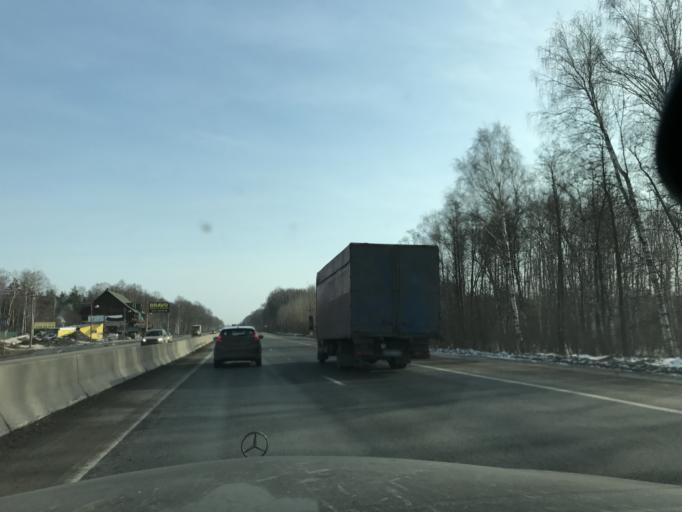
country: RU
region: Nizjnij Novgorod
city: Gorbatovka
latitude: 56.3076
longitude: 43.7120
